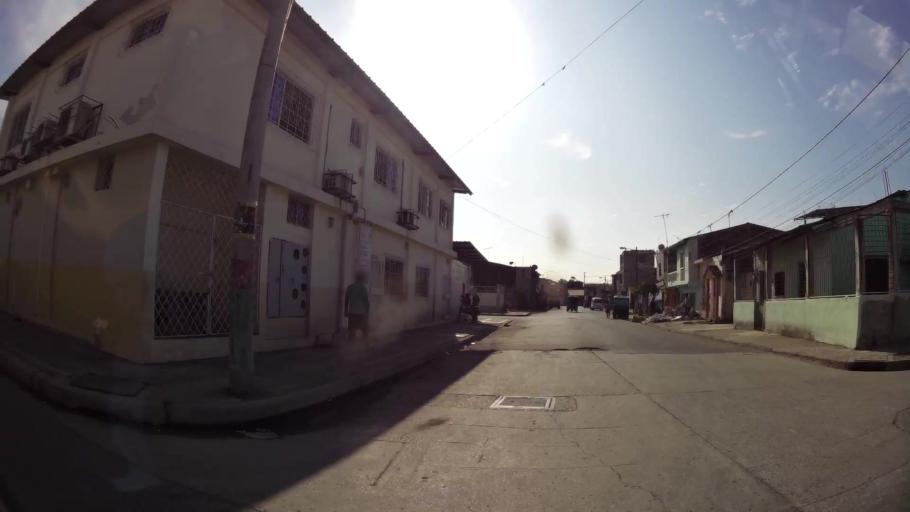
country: EC
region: Guayas
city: Eloy Alfaro
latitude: -2.0683
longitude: -79.9287
